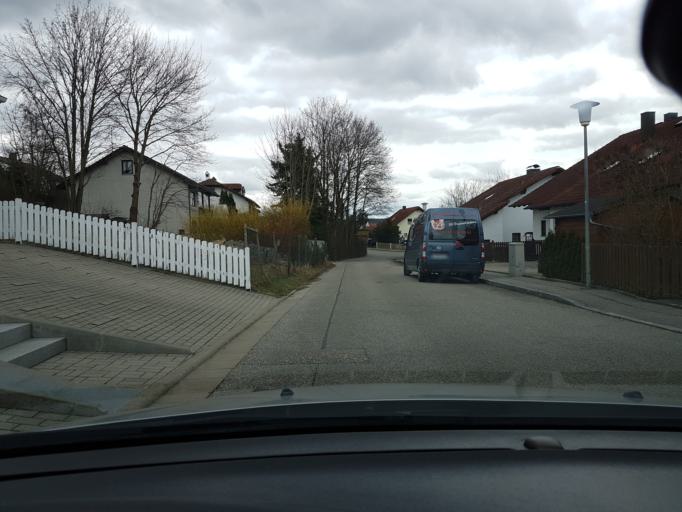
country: DE
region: Bavaria
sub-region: Lower Bavaria
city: Geisenhausen
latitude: 48.4798
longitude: 12.2520
